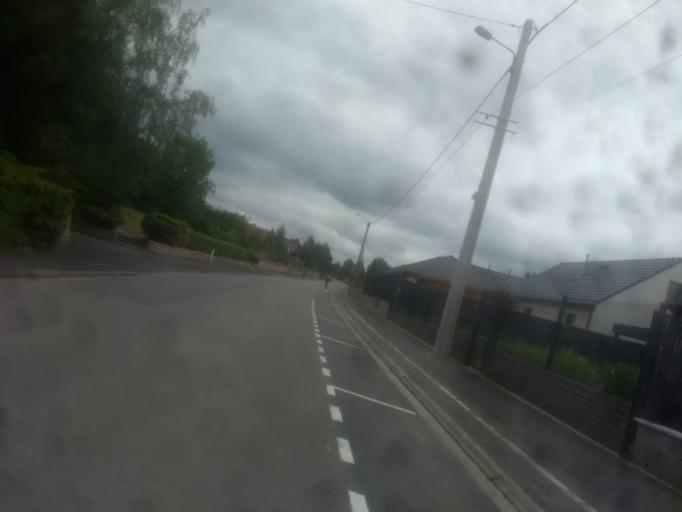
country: FR
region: Nord-Pas-de-Calais
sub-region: Departement du Pas-de-Calais
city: Saint-Nicolas
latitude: 50.3229
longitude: 2.7863
